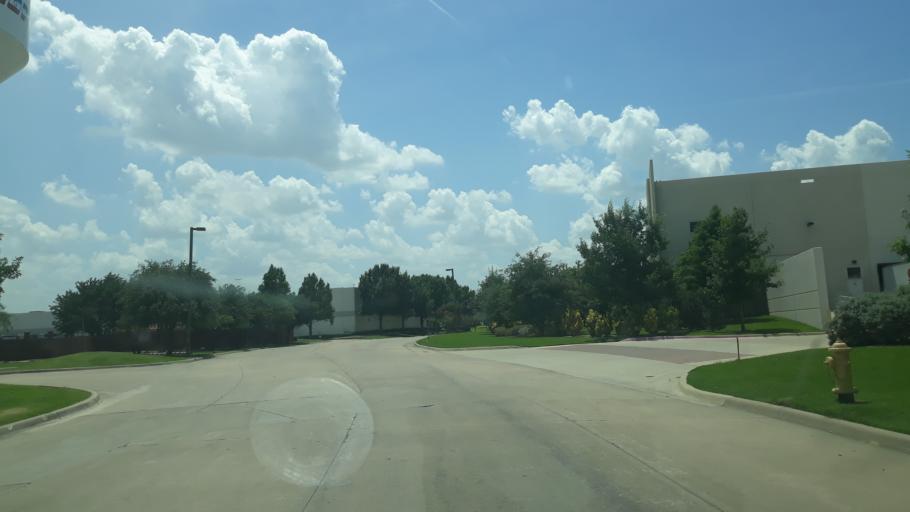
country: US
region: Texas
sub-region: Dallas County
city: Coppell
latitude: 32.9681
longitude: -97.0227
